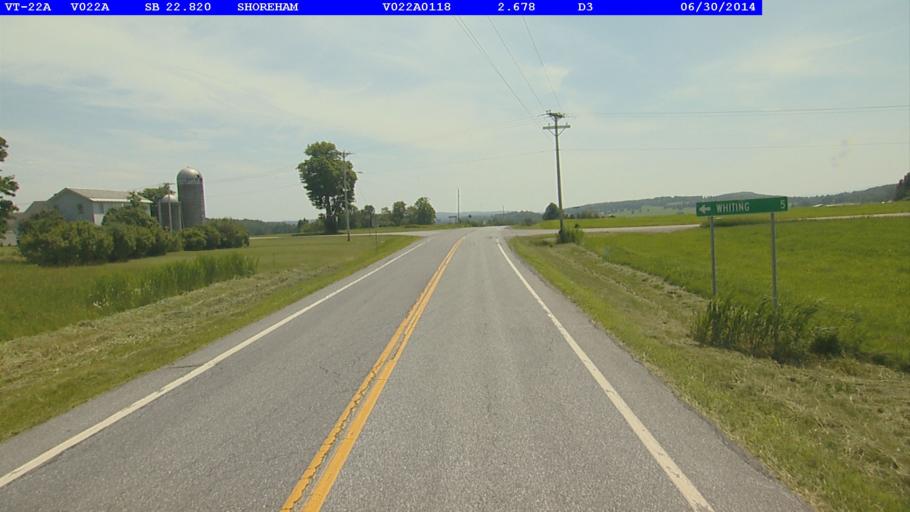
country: US
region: New York
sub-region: Essex County
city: Ticonderoga
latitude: 43.8881
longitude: -73.3095
